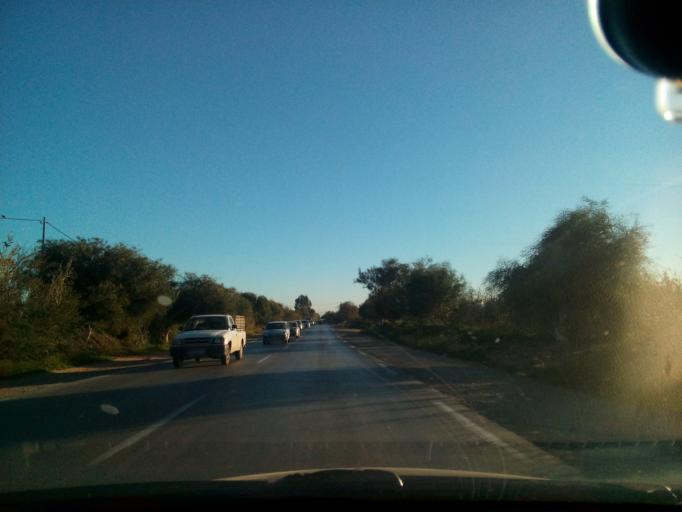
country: DZ
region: Mostaganem
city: Mostaganem
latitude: 35.8233
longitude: 0.1694
